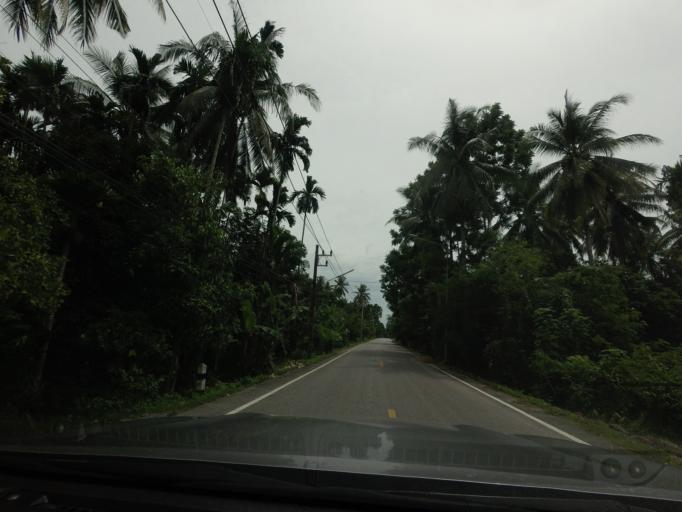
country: TH
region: Pattani
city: Kapho
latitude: 6.5621
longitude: 101.5336
